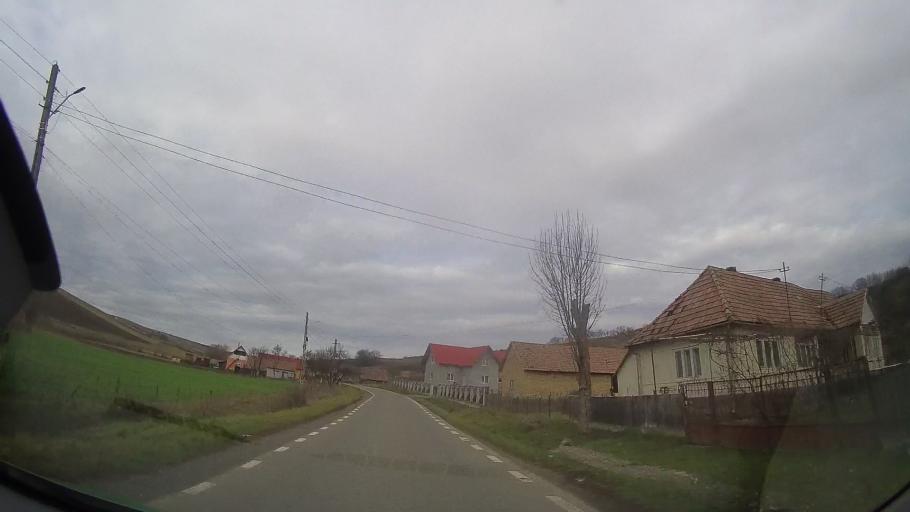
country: RO
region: Mures
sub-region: Comuna Cozma
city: Cozma
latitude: 46.8133
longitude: 24.4984
